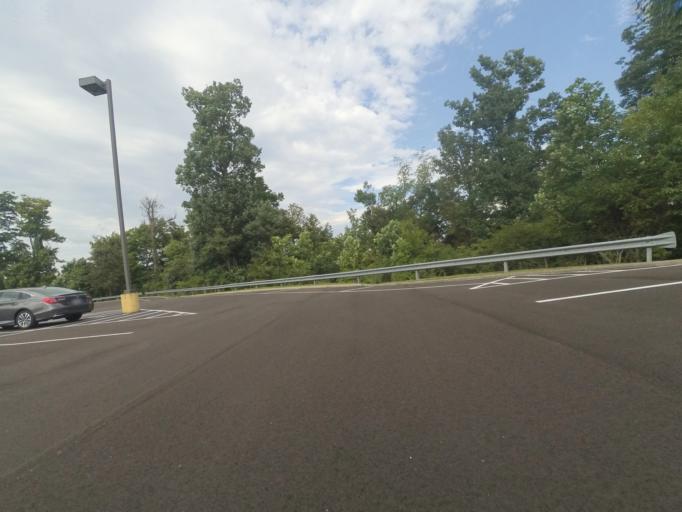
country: US
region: West Virginia
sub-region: Cabell County
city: Huntington
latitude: 38.3916
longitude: -82.4571
